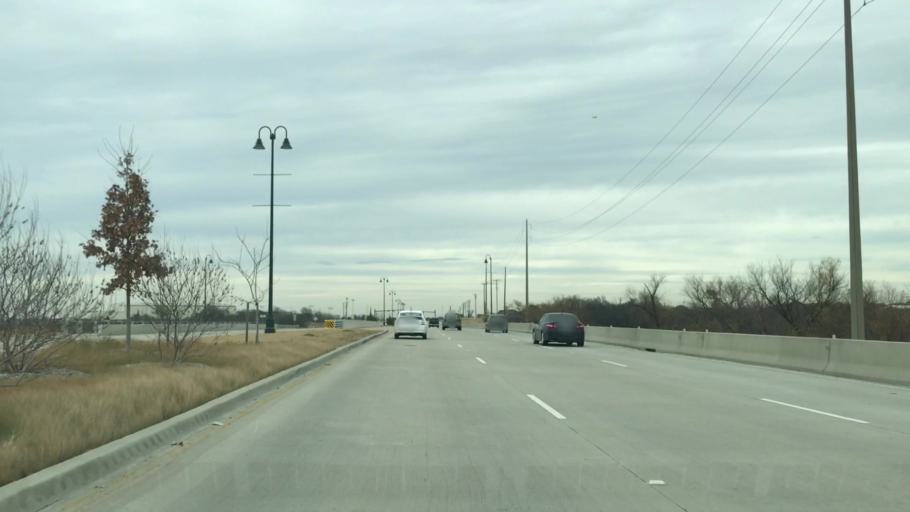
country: US
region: Texas
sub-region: Denton County
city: The Colony
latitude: 33.1083
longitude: -96.8920
